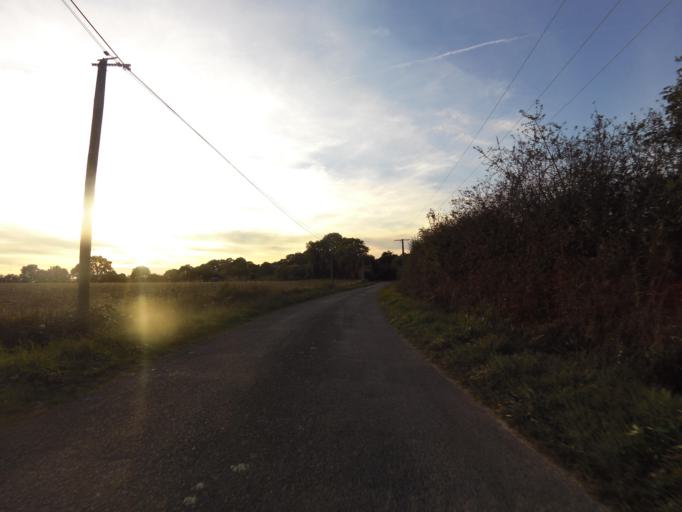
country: FR
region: Brittany
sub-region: Departement du Morbihan
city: Sene
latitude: 47.6327
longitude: -2.6956
